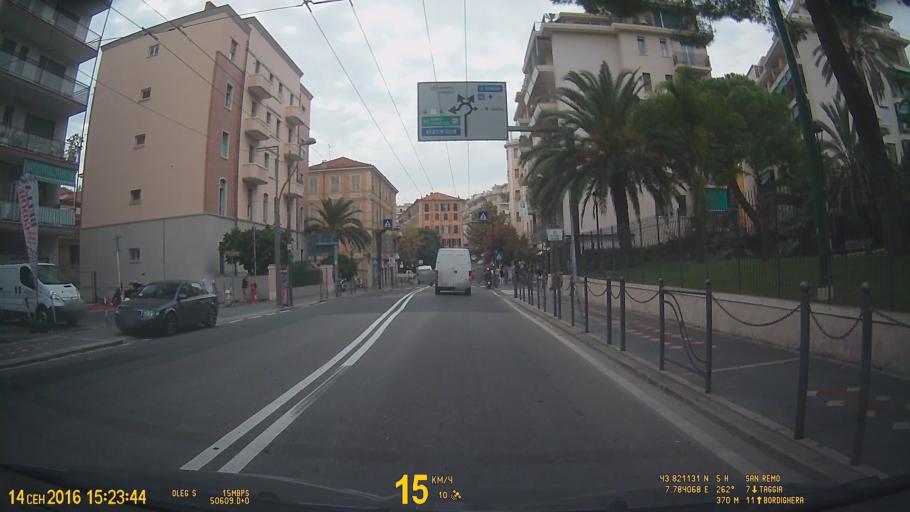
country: IT
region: Liguria
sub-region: Provincia di Imperia
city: San Remo
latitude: 43.8214
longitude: 7.7856
